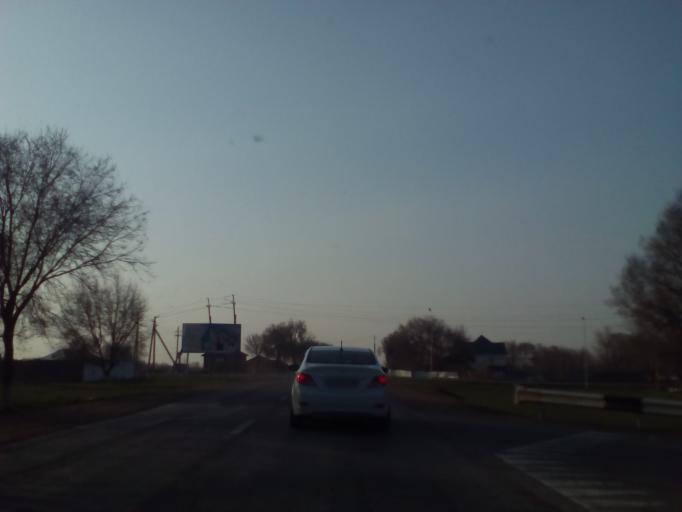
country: KZ
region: Almaty Oblysy
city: Burunday
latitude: 43.1741
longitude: 76.5271
